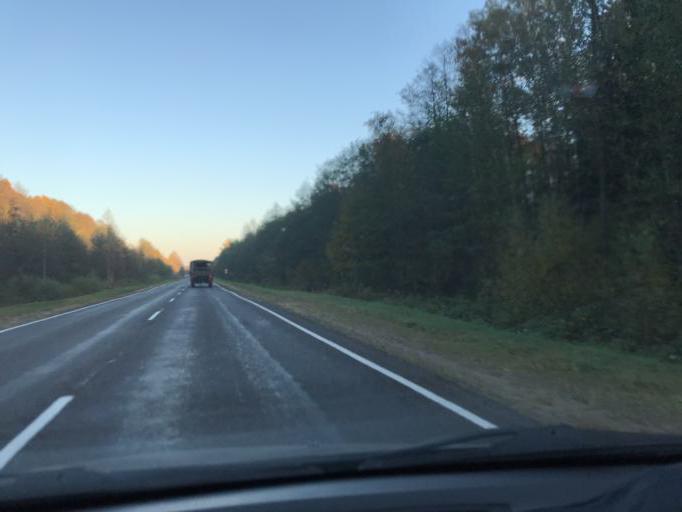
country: BY
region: Minsk
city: Staryya Darohi
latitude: 53.0433
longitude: 28.1405
